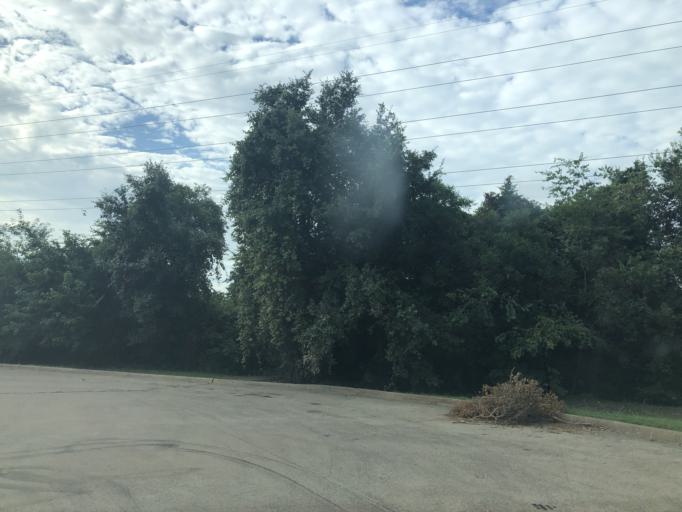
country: US
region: Texas
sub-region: Dallas County
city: Irving
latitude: 32.8148
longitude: -96.8945
